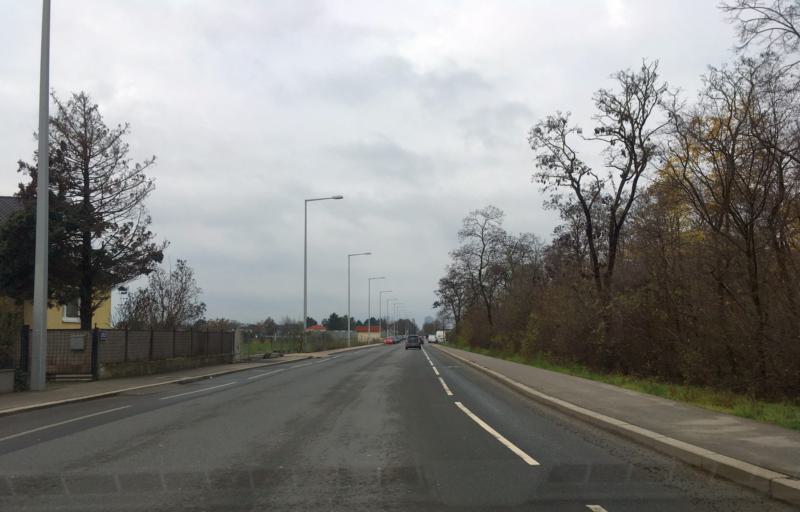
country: AT
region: Lower Austria
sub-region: Politischer Bezirk Ganserndorf
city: Aderklaa
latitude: 48.2548
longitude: 16.4966
